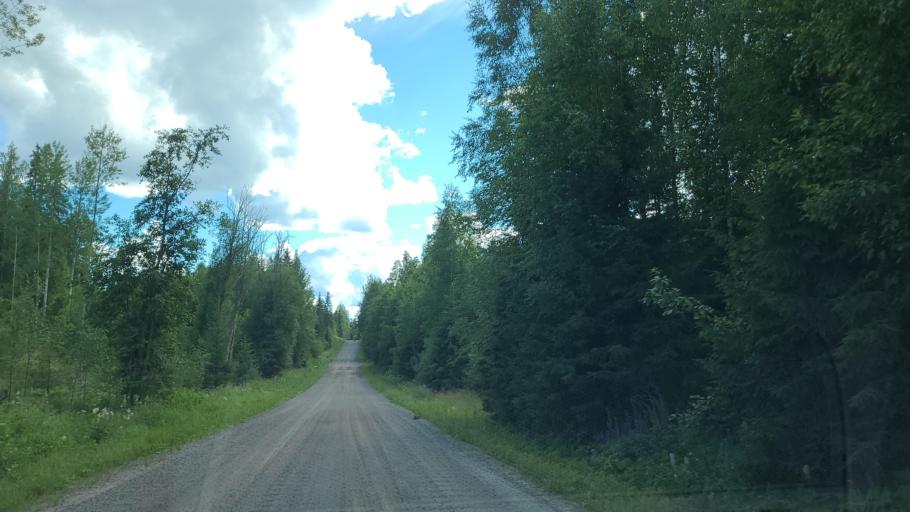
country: FI
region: Central Finland
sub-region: Jaemsae
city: Jaemsae
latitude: 61.9141
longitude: 25.3027
